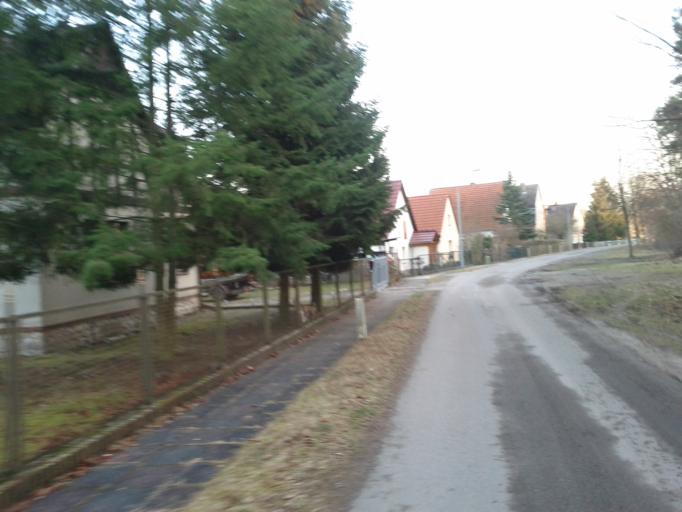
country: DE
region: Brandenburg
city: Grunheide
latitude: 52.4227
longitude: 13.7933
